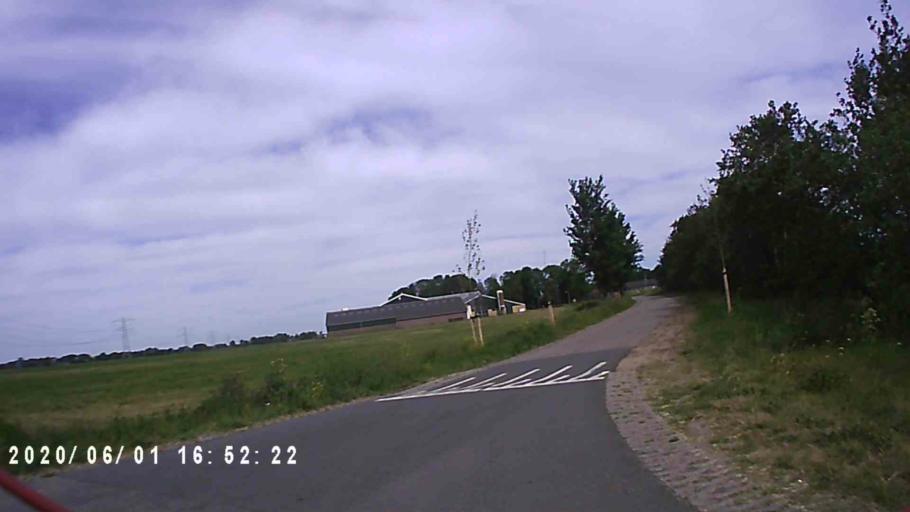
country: NL
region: Friesland
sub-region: Gemeente Tytsjerksteradiel
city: Tytsjerk
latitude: 53.1895
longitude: 5.9159
